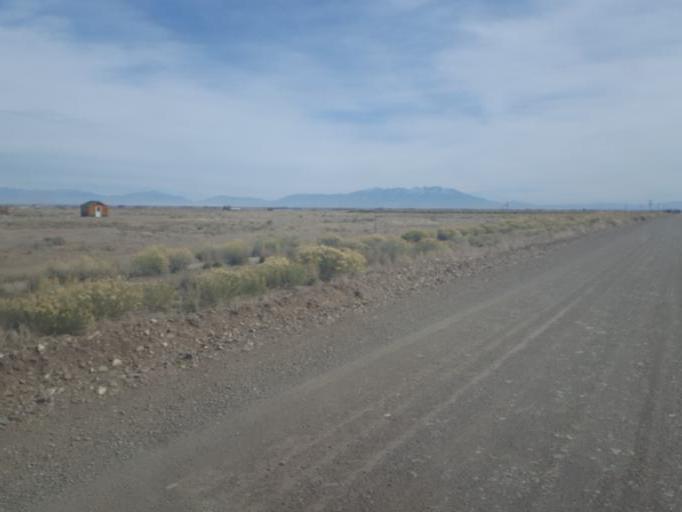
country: US
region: Colorado
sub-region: Rio Grande County
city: Monte Vista
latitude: 37.4011
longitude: -106.1170
